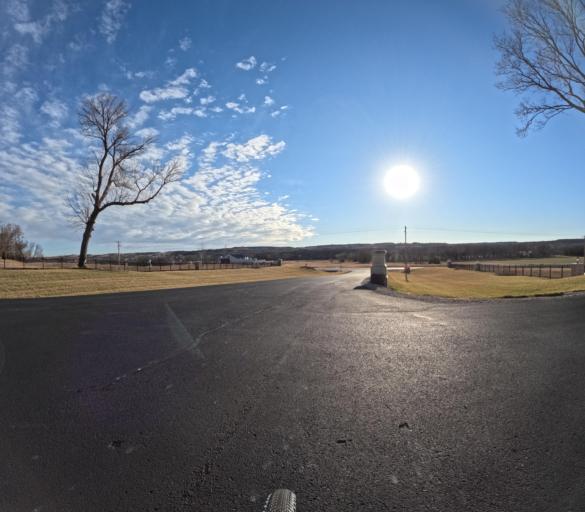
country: US
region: Kansas
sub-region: Riley County
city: Manhattan
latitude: 39.1987
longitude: -96.6526
